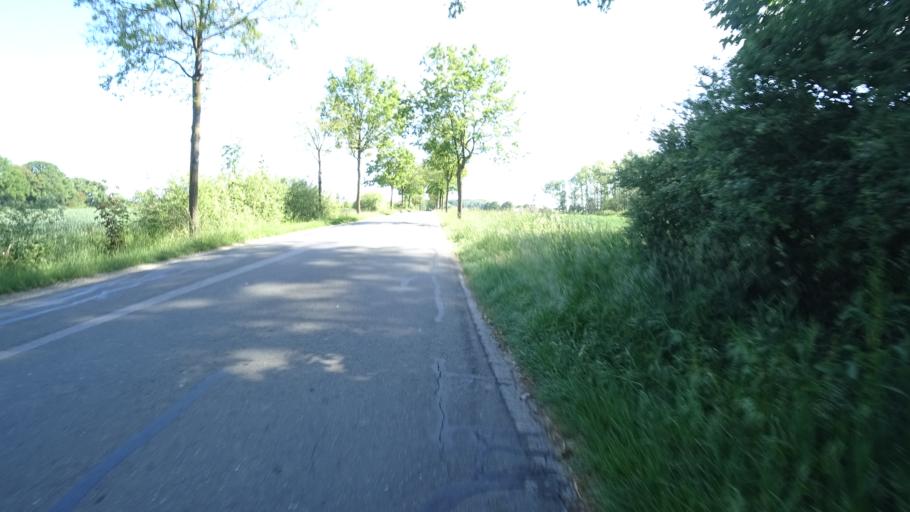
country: DE
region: North Rhine-Westphalia
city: Oelde
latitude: 51.8182
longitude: 8.2218
